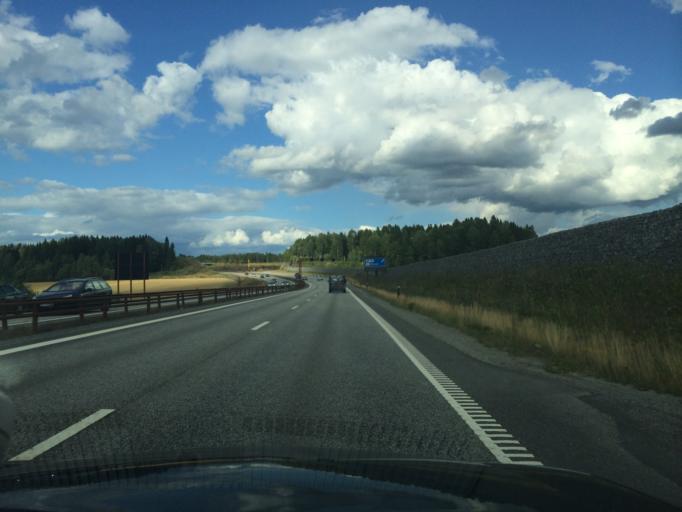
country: NO
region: Akershus
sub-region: Eidsvoll
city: Raholt
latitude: 60.3268
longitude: 11.1836
